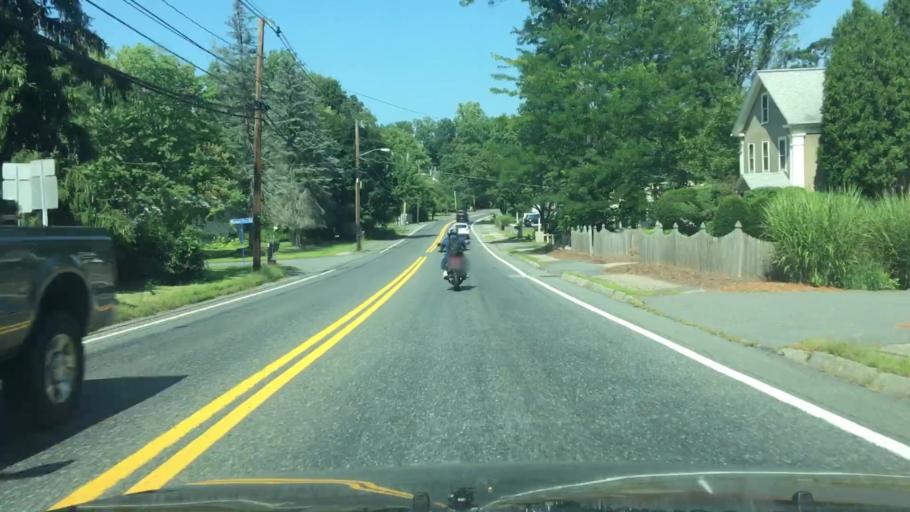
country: US
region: Massachusetts
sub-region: Middlesex County
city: Holliston
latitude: 42.1941
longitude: -71.4353
